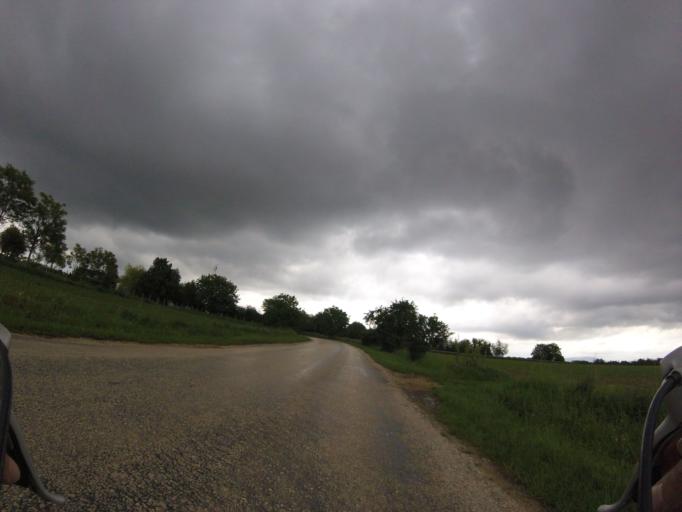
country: HU
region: Baranya
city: Pellerd
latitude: 45.9683
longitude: 18.1626
